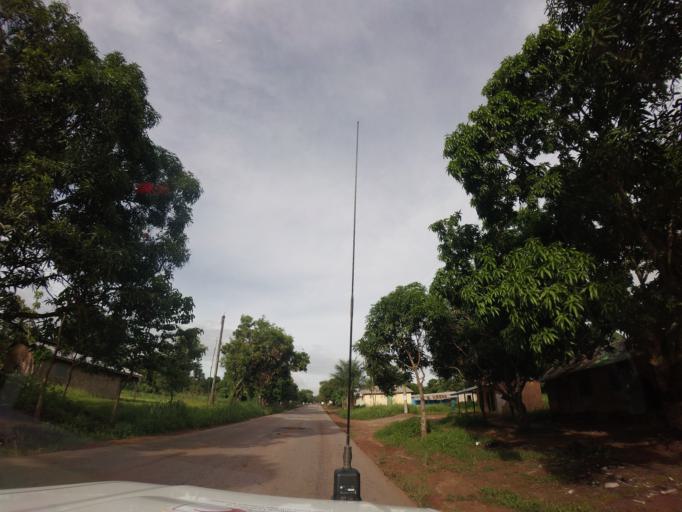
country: GN
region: Kindia
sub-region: Kindia
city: Kindia
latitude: 9.9245
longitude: -12.9924
